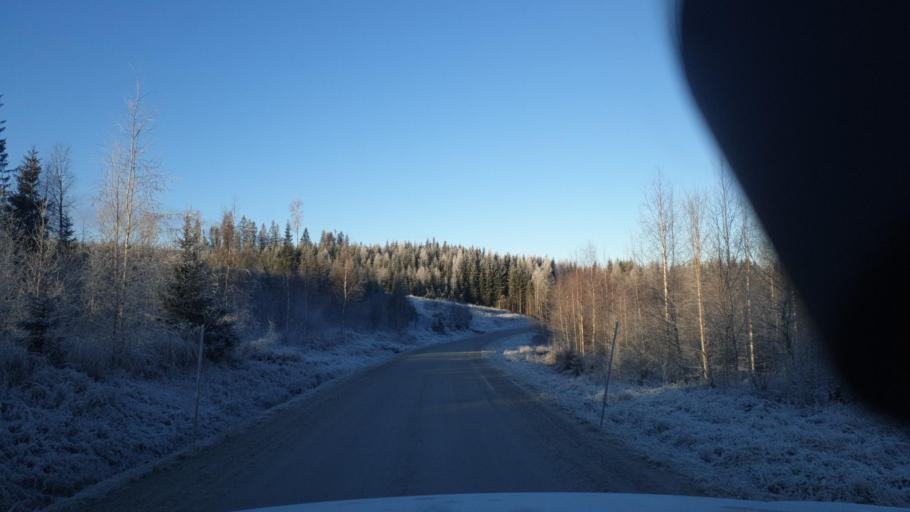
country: SE
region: Vaermland
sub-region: Arvika Kommun
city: Arvika
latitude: 59.7942
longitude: 12.7524
